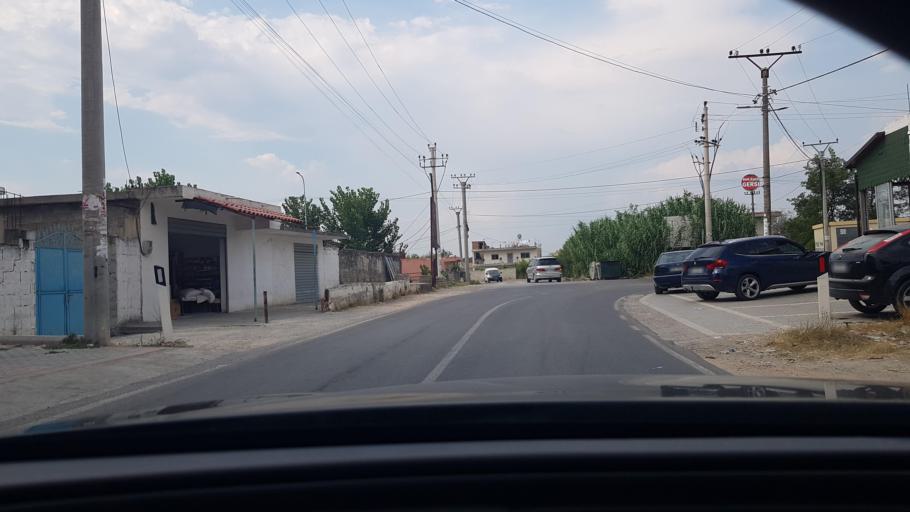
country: AL
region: Durres
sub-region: Rrethi i Durresit
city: Katundi i Ri
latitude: 41.4260
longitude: 19.5478
